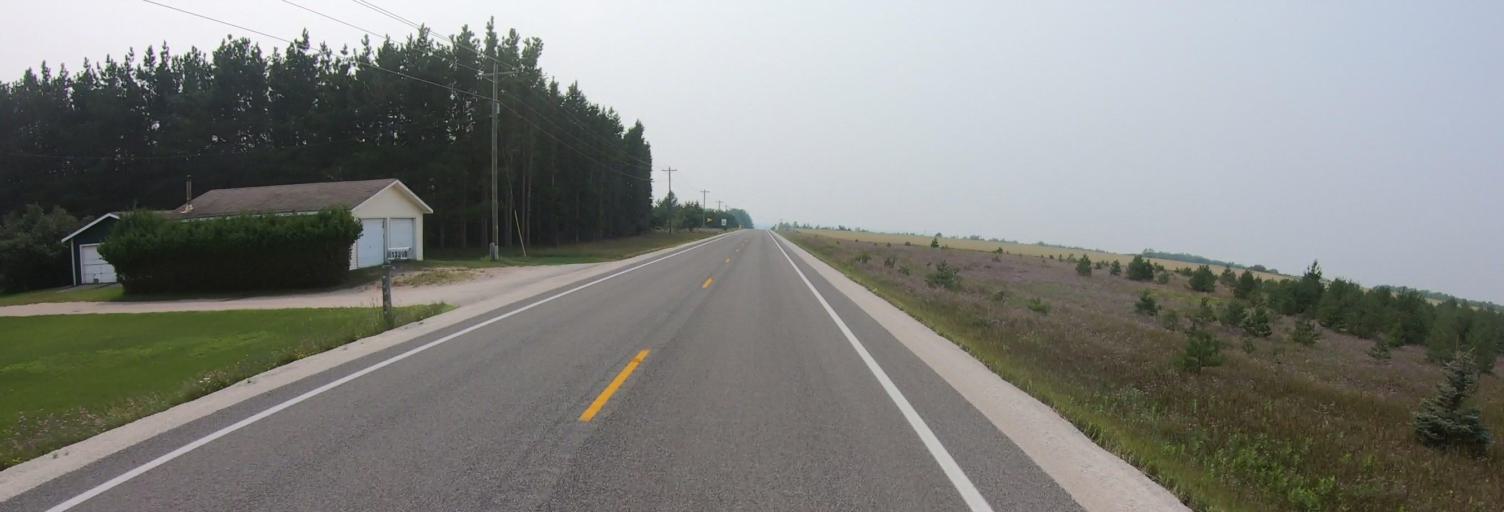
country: US
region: Michigan
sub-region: Chippewa County
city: Sault Ste. Marie
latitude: 46.0721
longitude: -84.1684
